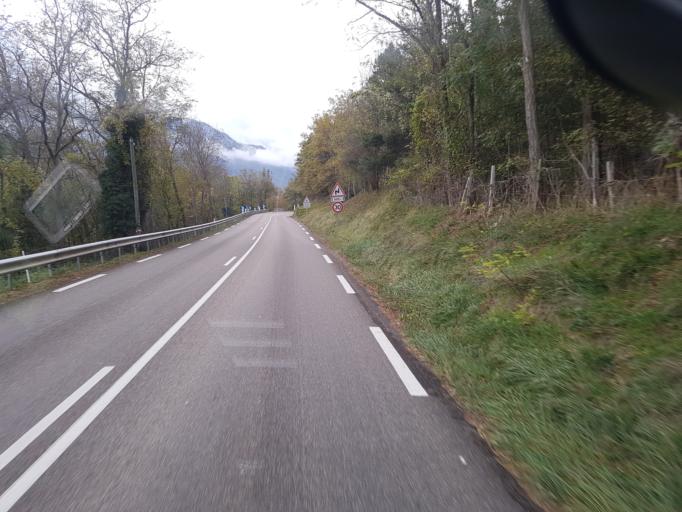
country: FR
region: Rhone-Alpes
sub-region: Departement de l'Isere
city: Le Gua
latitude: 44.9625
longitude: 5.6363
